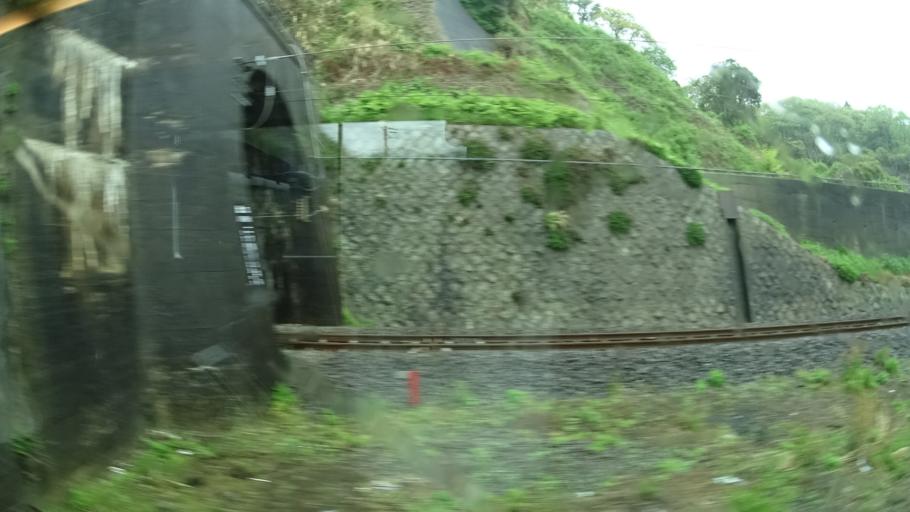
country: JP
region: Ibaraki
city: Kitaibaraki
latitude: 36.8085
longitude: 140.7616
